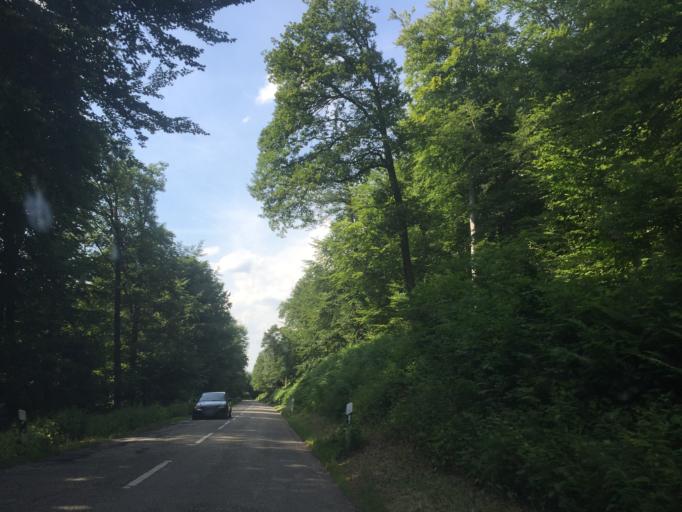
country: DE
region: Baden-Wuerttemberg
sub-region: Karlsruhe Region
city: Heidelberg
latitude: 49.3899
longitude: 8.7155
